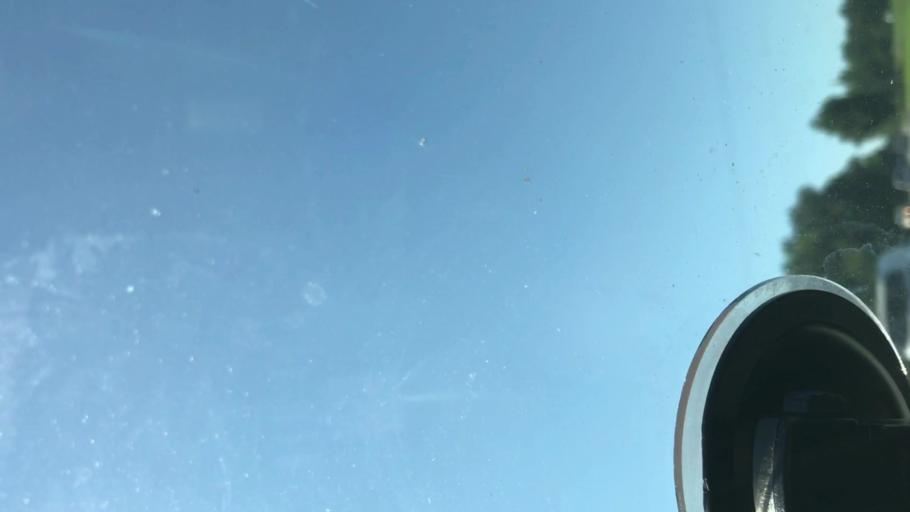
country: US
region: Virginia
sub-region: Spotsylvania County
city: Spotsylvania Courthouse
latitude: 38.1687
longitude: -77.5192
